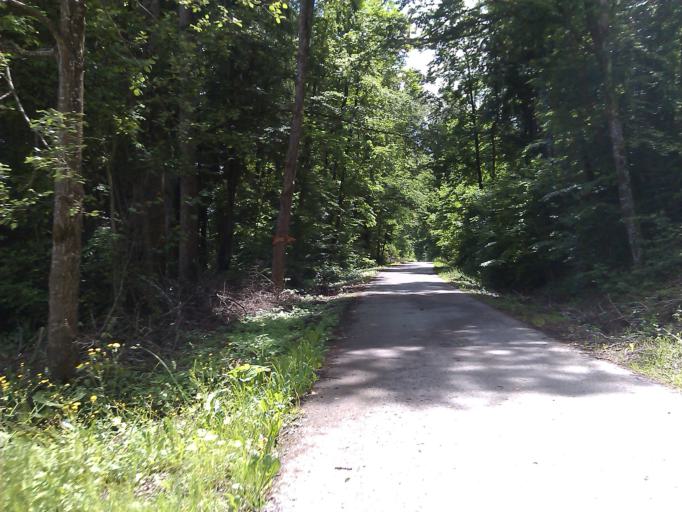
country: DE
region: Bavaria
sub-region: Swabia
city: Biessenhofen
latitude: 47.8579
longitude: 10.6314
